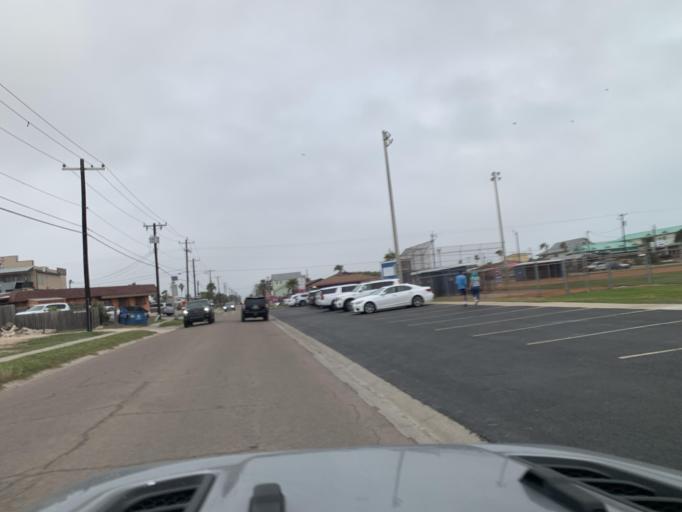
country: US
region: Texas
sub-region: Nueces County
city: Port Aransas
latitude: 27.8328
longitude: -97.0598
